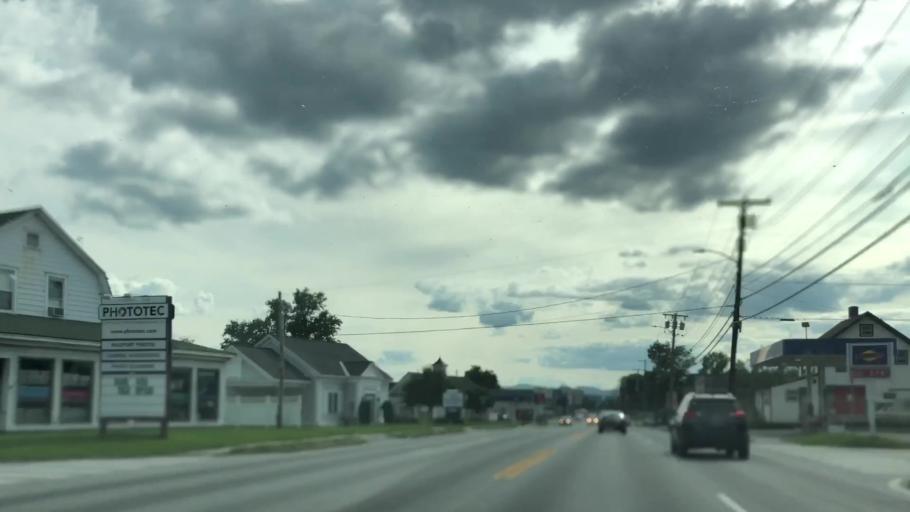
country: US
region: Vermont
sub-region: Rutland County
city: Rutland
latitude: 43.6140
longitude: -72.9633
